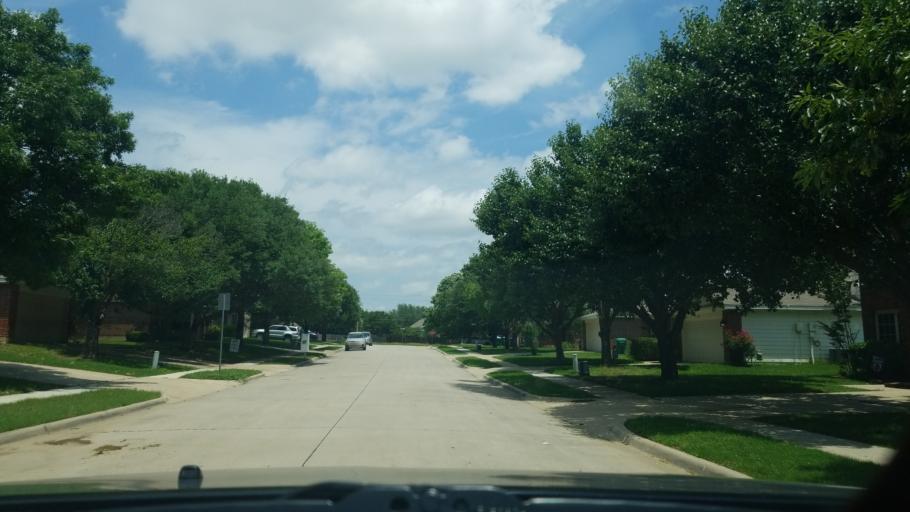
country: US
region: Texas
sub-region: Denton County
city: Denton
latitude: 33.2385
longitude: -97.1672
